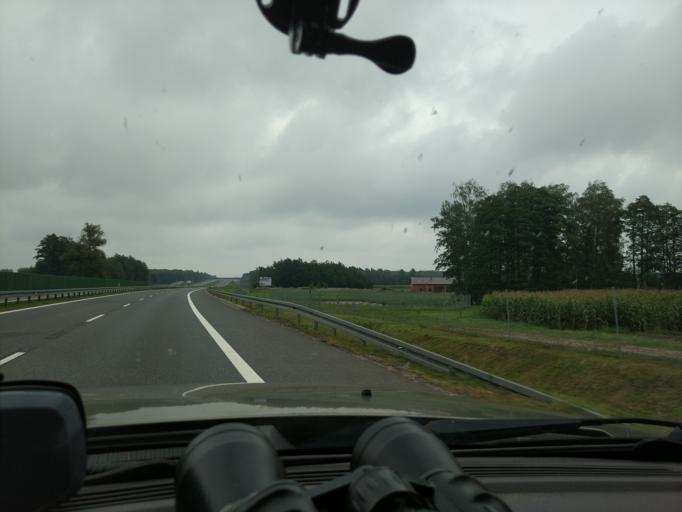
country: PL
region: Podlasie
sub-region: Powiat zambrowski
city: Zambrow
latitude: 53.0187
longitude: 22.3132
